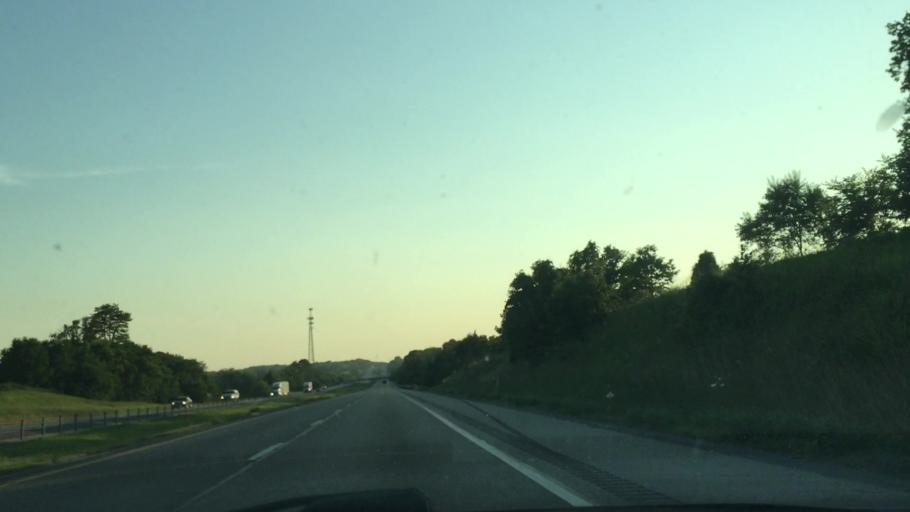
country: US
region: Indiana
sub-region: Switzerland County
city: Vevay
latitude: 38.6649
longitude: -85.0279
